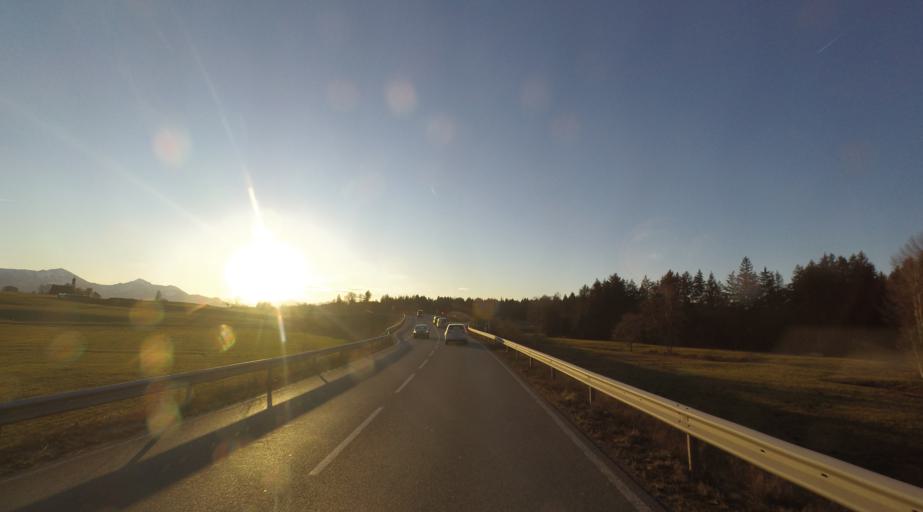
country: DE
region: Bavaria
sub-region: Upper Bavaria
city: Traunstein
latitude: 47.8809
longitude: 12.6609
